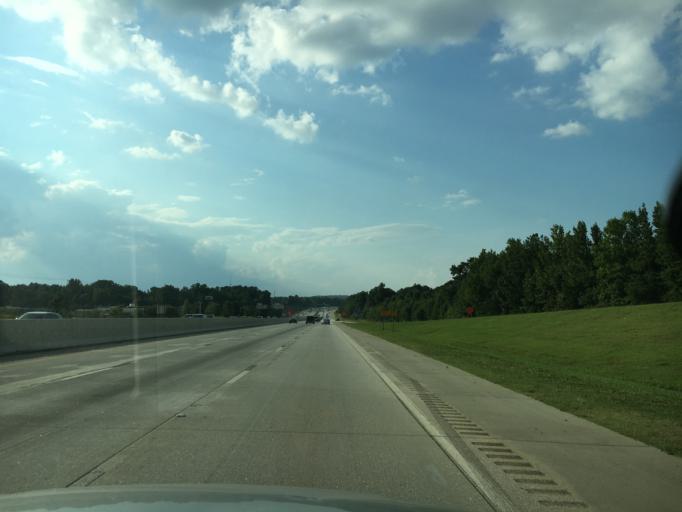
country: US
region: South Carolina
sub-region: Greenville County
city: Mauldin
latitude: 34.8065
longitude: -82.2833
